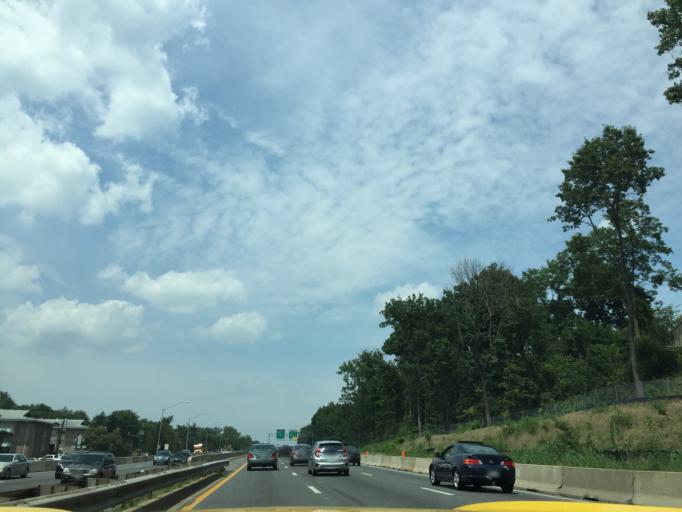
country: US
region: Maryland
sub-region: Prince George's County
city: Oxon Hill
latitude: 38.7882
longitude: -76.9983
